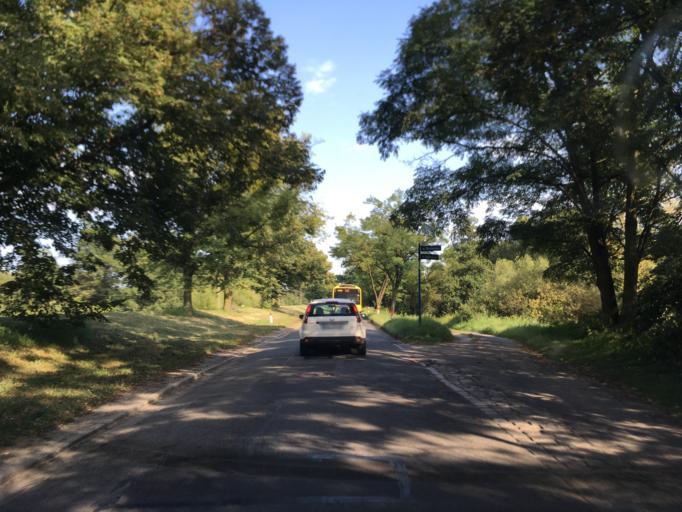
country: PL
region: Lower Silesian Voivodeship
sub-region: Powiat wroclawski
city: Radwanice
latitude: 51.0931
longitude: 17.0875
